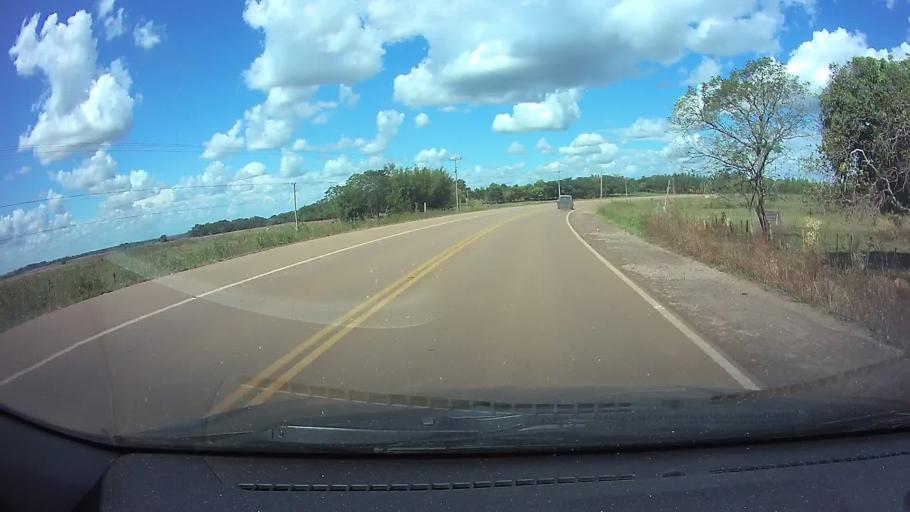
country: PY
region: Paraguari
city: La Colmena
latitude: -25.9137
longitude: -56.7141
